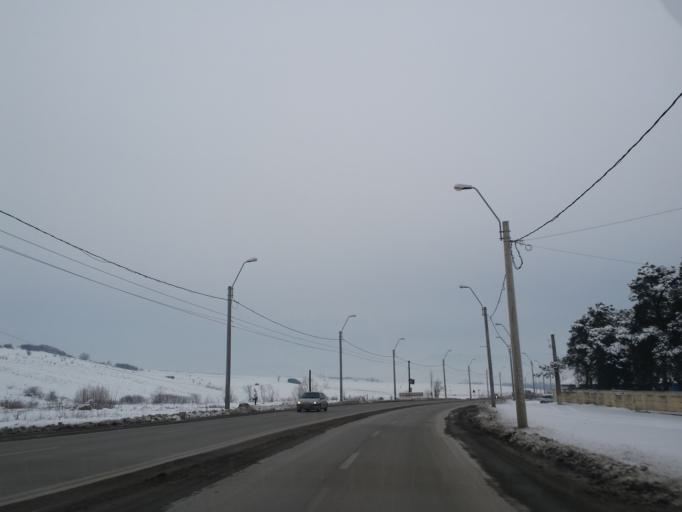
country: RO
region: Hunedoara
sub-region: Municipiul Deva
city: Cristur
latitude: 45.8434
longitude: 22.9481
